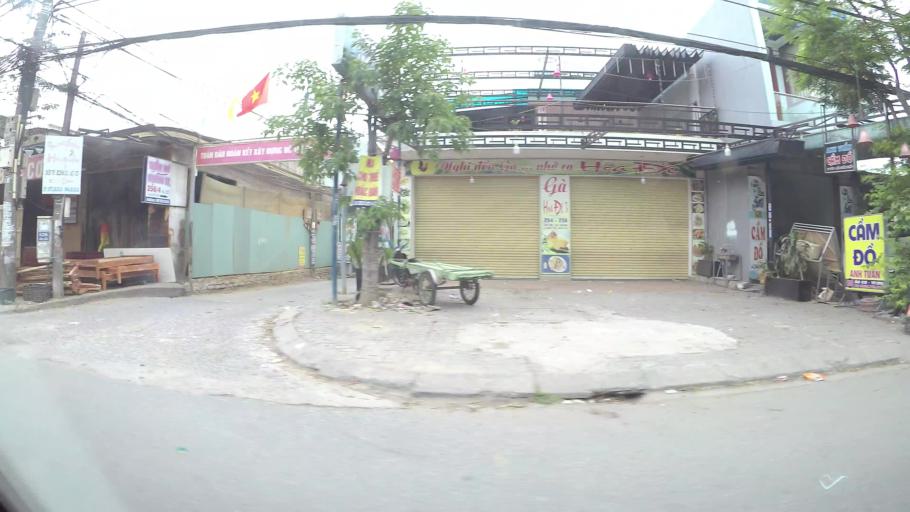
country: VN
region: Da Nang
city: Lien Chieu
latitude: 16.0713
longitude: 108.1431
